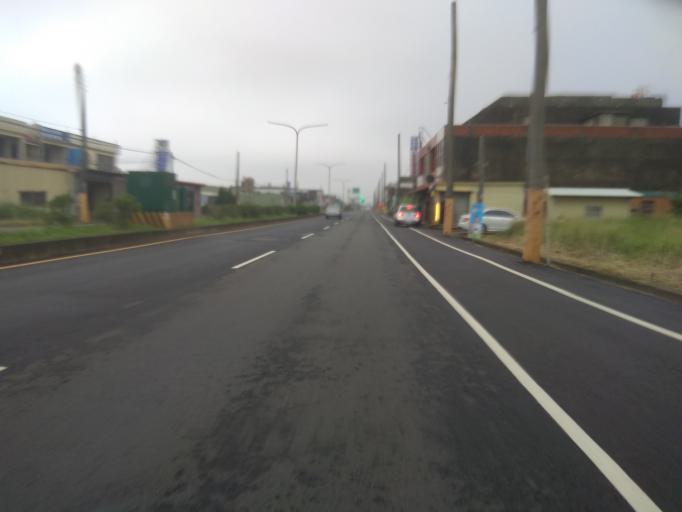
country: TW
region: Taiwan
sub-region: Hsinchu
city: Zhubei
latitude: 25.0283
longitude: 121.0665
